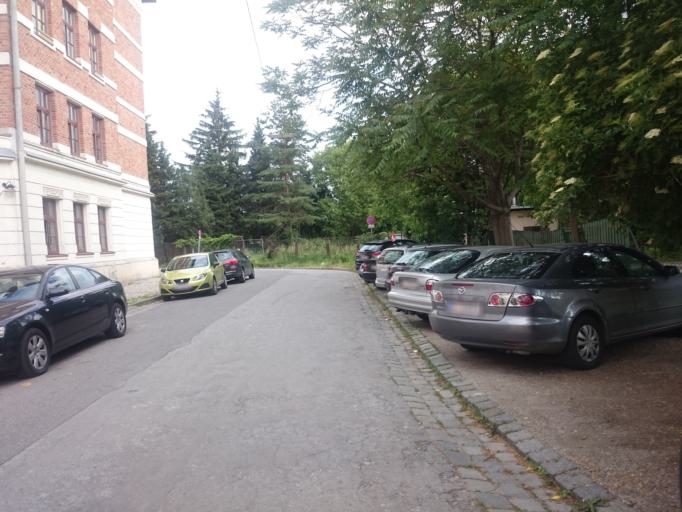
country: AT
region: Lower Austria
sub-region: Politischer Bezirk Wien-Umgebung
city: Gerasdorf bei Wien
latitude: 48.2606
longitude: 16.4155
